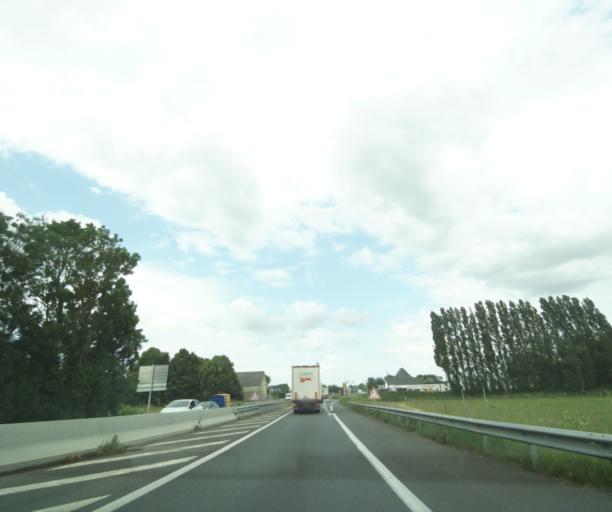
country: FR
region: Pays de la Loire
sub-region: Departement de Maine-et-Loire
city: Vivy
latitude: 47.3029
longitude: -0.0369
